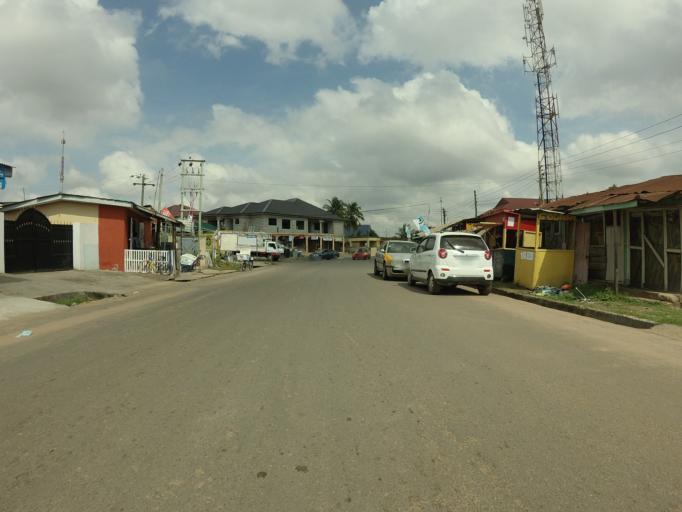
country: GH
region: Greater Accra
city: Nungua
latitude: 5.6155
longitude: -0.0848
